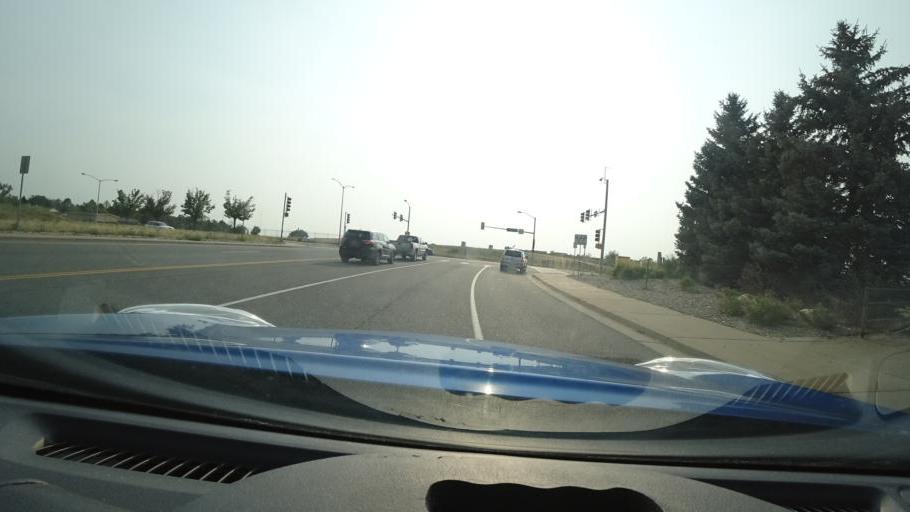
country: US
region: Colorado
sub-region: Adams County
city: Aurora
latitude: 39.6660
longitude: -104.8092
